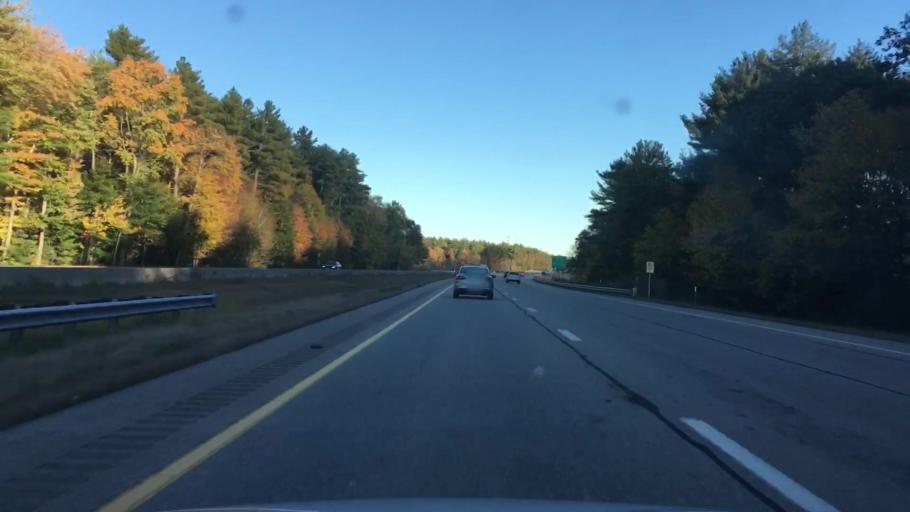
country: US
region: New Hampshire
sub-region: Rockingham County
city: Epping
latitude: 43.0253
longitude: -71.0673
